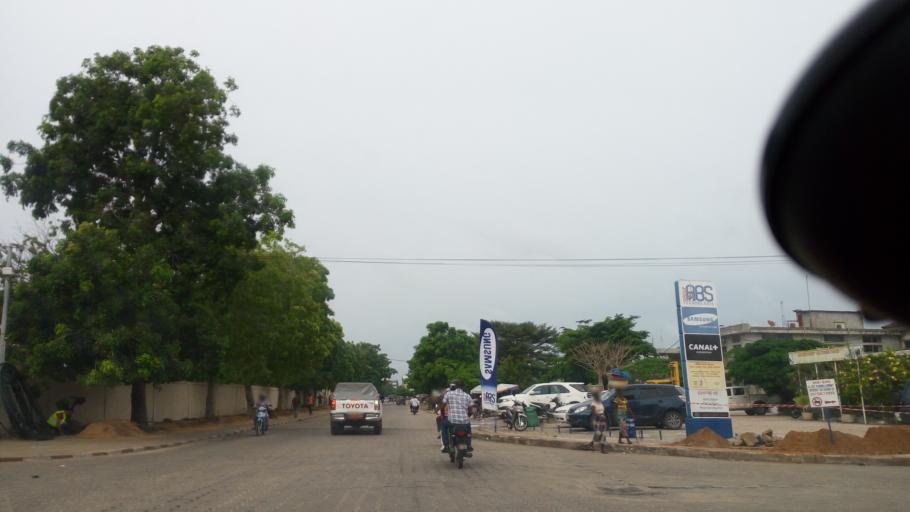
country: BJ
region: Littoral
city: Cotonou
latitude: 6.3563
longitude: 2.4151
